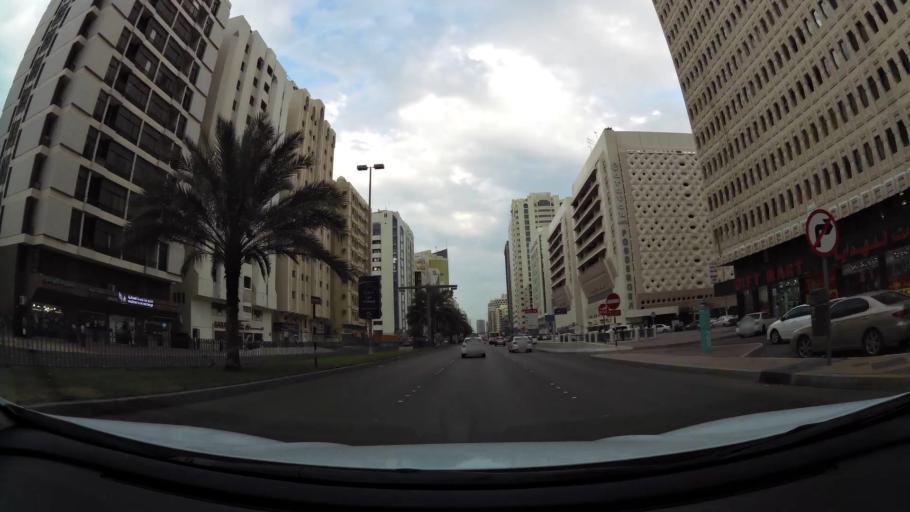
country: AE
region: Abu Dhabi
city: Abu Dhabi
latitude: 24.4848
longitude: 54.3618
